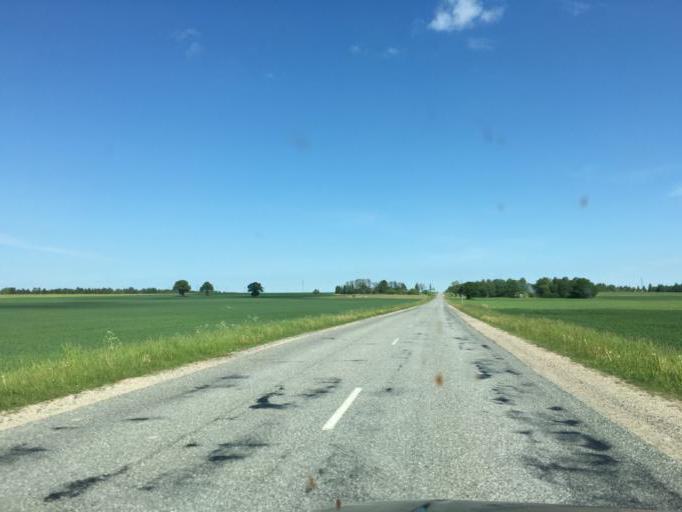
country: LV
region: Talsu Rajons
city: Valdemarpils
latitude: 57.3509
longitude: 22.4972
